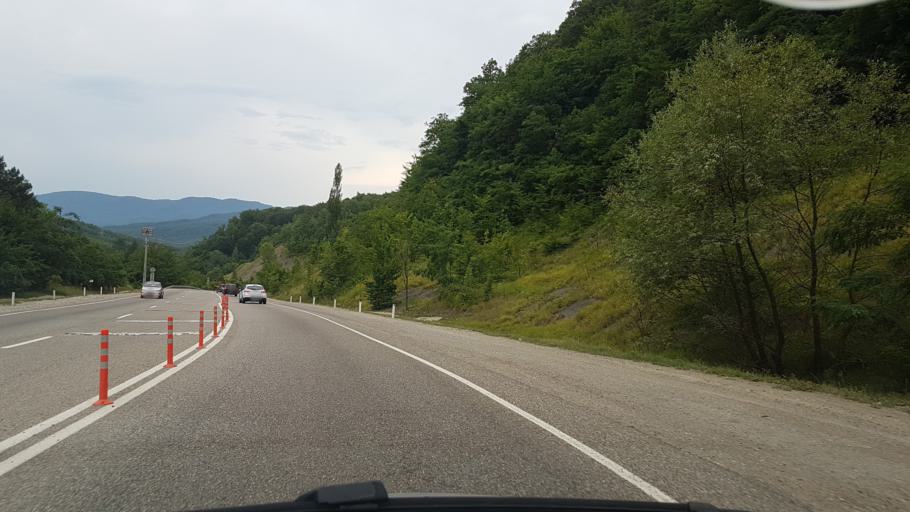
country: RU
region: Krasnodarskiy
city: Novomikhaylovskiy
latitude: 44.4932
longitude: 38.8979
